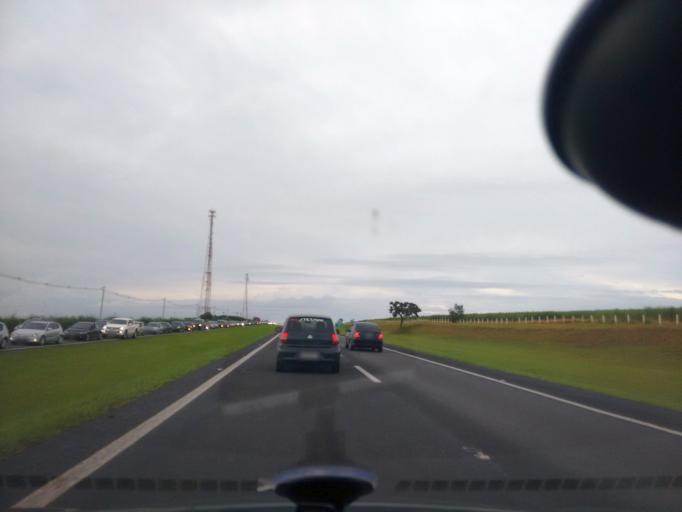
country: BR
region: Sao Paulo
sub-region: Itirapina
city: Itirapina
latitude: -22.1949
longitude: -47.7756
